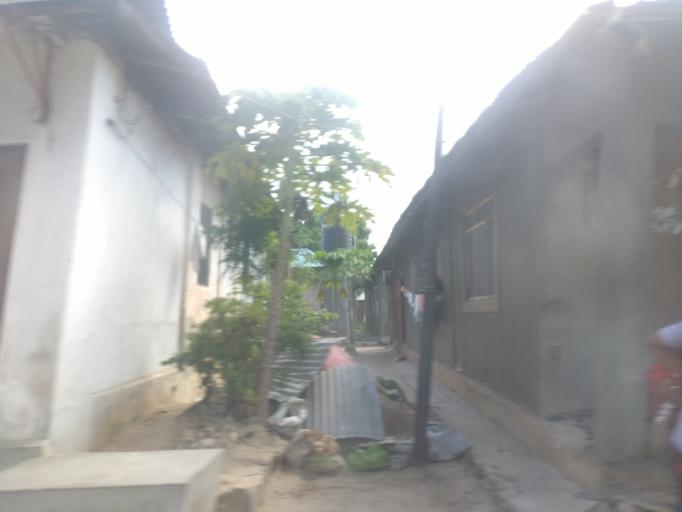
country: TZ
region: Zanzibar Urban/West
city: Zanzibar
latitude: -6.1696
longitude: 39.2048
